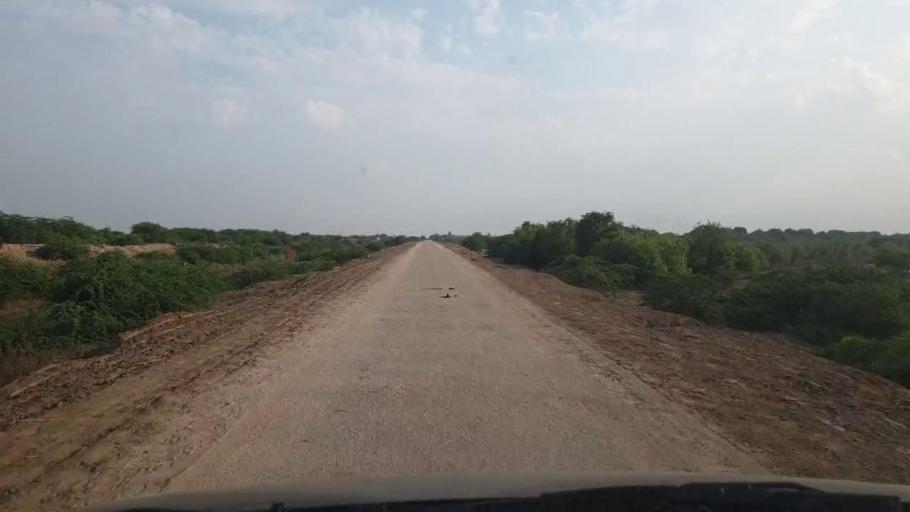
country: PK
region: Sindh
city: Badin
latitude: 24.5348
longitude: 68.6766
